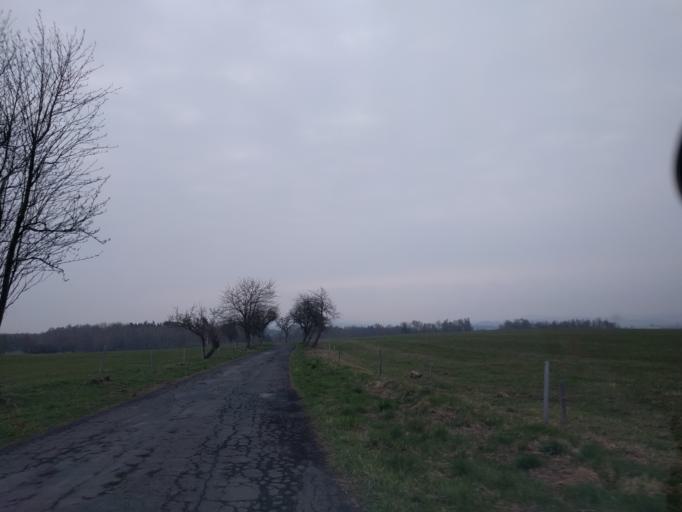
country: CZ
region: Karlovarsky
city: Bochov
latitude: 50.1229
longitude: 13.0851
